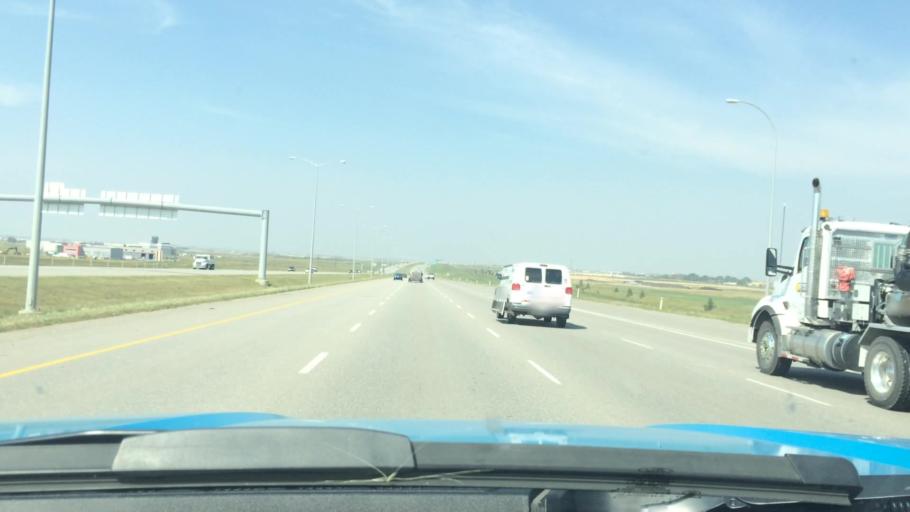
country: CA
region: Alberta
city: Chestermere
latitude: 50.9536
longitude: -113.9204
